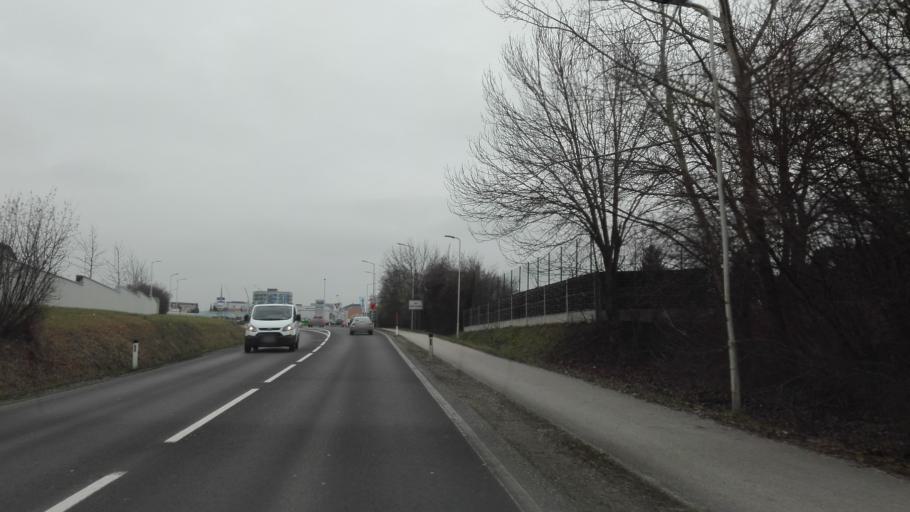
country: AT
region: Upper Austria
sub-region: Politischer Bezirk Linz-Land
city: Leonding
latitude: 48.2691
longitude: 14.2563
